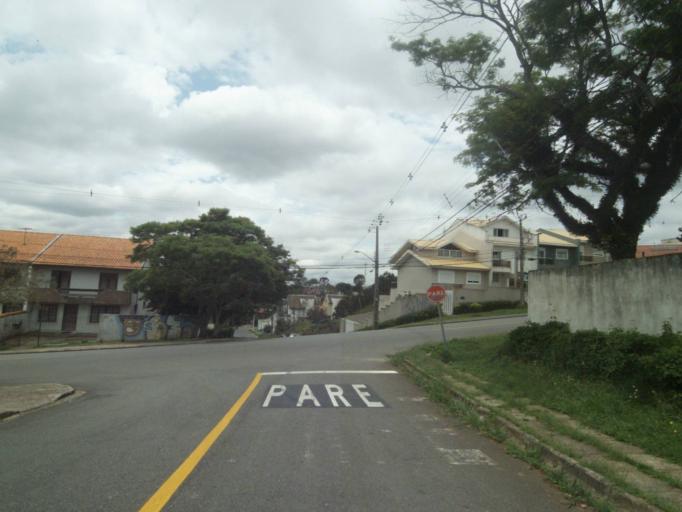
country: BR
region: Parana
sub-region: Curitiba
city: Curitiba
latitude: -25.3922
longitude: -49.2877
